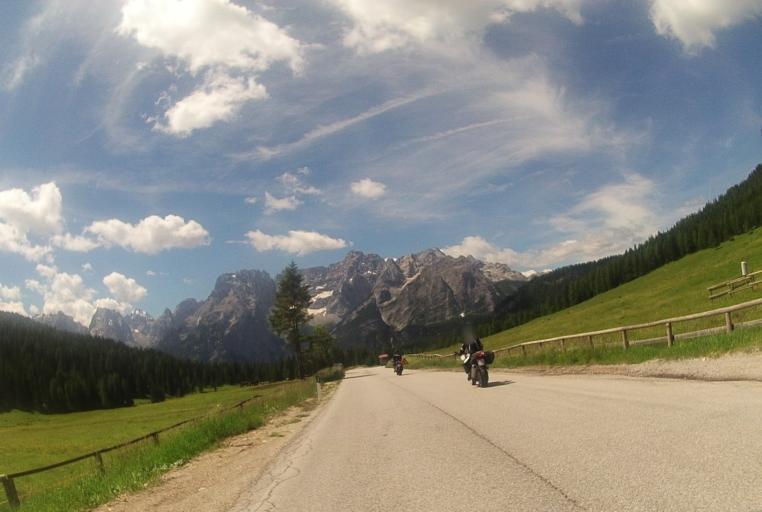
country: IT
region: Veneto
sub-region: Provincia di Belluno
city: Cortina d'Ampezzo
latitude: 46.5766
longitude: 12.2507
